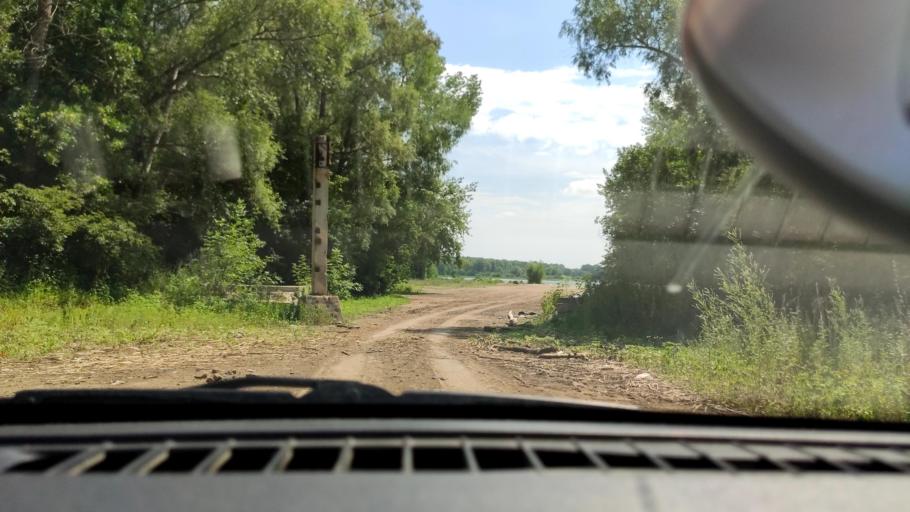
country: RU
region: Samara
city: Smyshlyayevka
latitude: 53.2045
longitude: 50.3216
